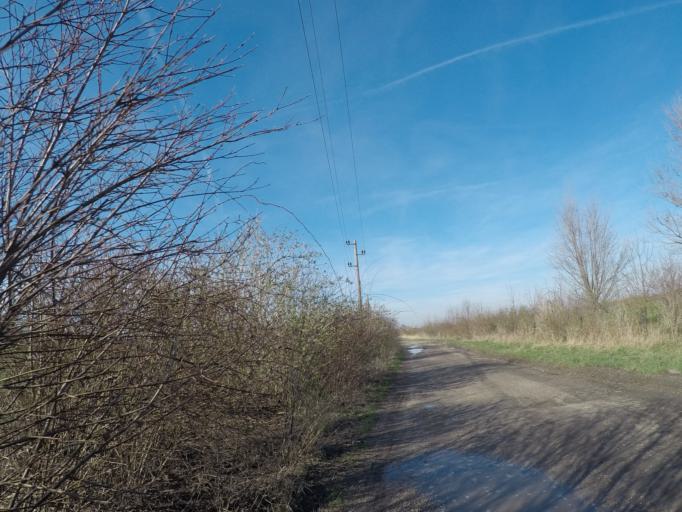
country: AT
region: Lower Austria
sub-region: Politischer Bezirk Modling
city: Biedermannsdorf
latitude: 48.0927
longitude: 16.3308
